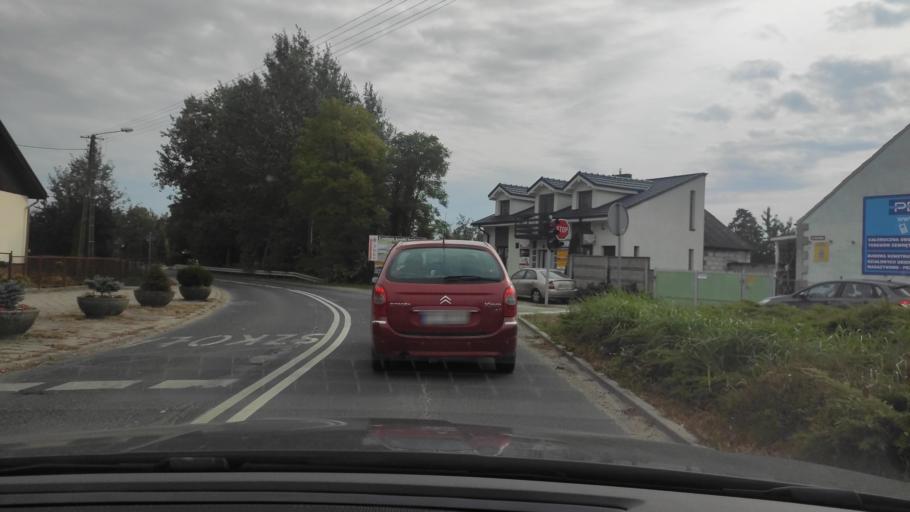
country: PL
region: Greater Poland Voivodeship
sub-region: Powiat poznanski
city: Kleszczewo
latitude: 52.3809
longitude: 17.1631
